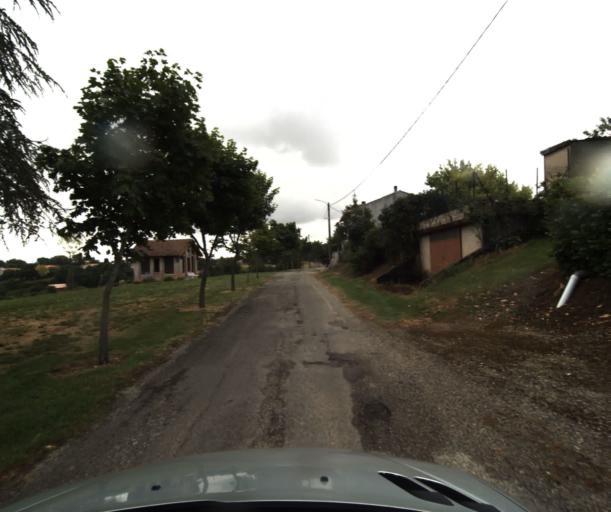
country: FR
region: Midi-Pyrenees
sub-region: Departement du Tarn-et-Garonne
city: Lavit
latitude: 43.9560
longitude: 0.9208
